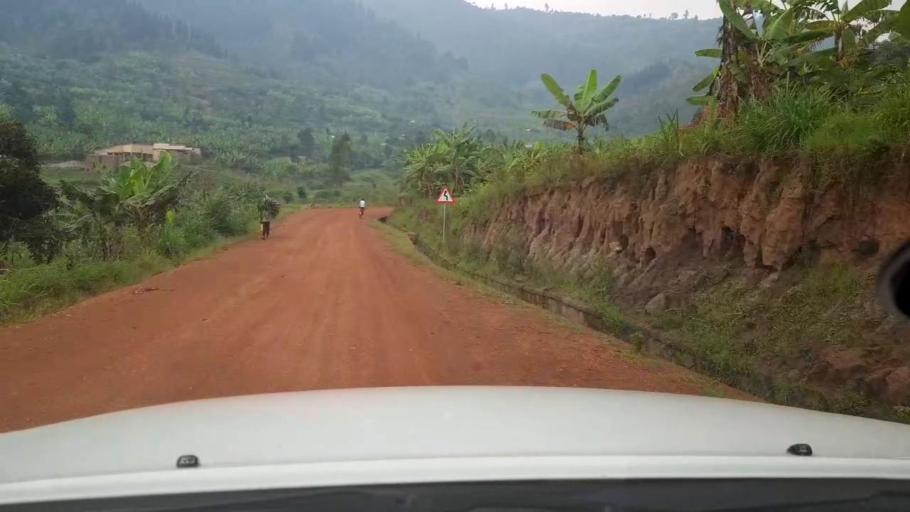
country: RW
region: Kigali
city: Kigali
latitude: -1.8536
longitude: 29.9040
